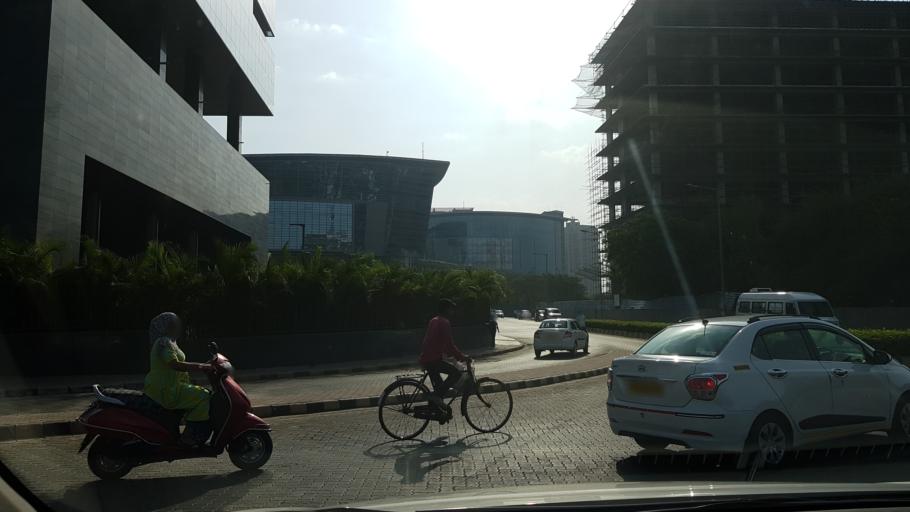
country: IN
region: Maharashtra
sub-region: Pune Division
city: Lohogaon
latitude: 18.5501
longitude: 73.9474
